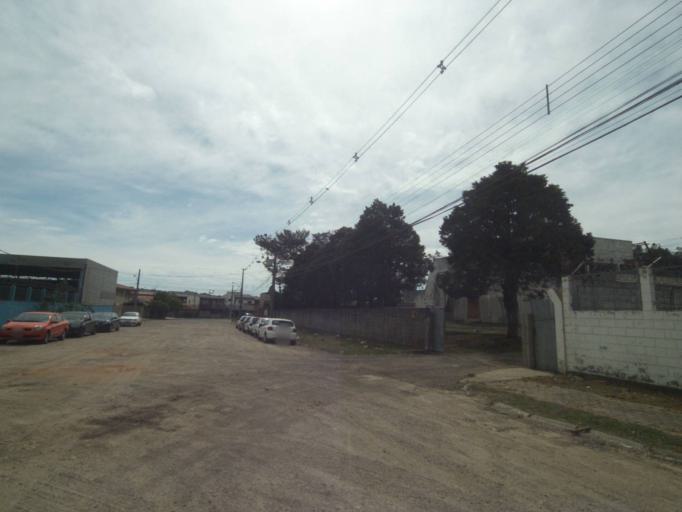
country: BR
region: Parana
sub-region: Araucaria
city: Araucaria
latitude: -25.5186
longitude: -49.3328
